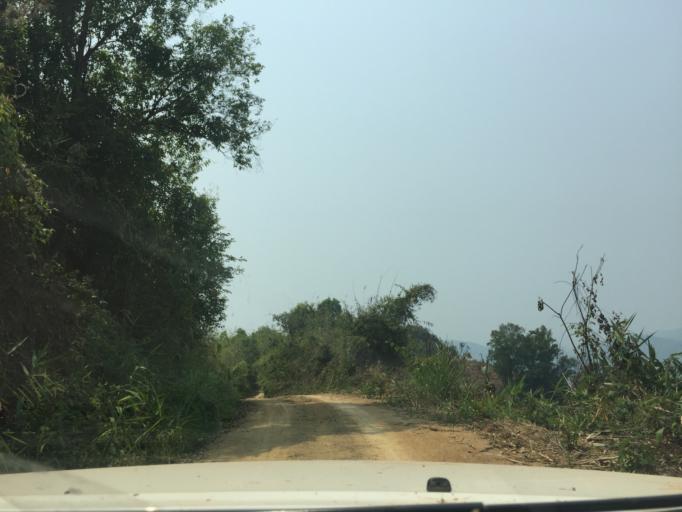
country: LA
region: Loungnamtha
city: Muang Nale
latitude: 20.6282
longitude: 101.6300
